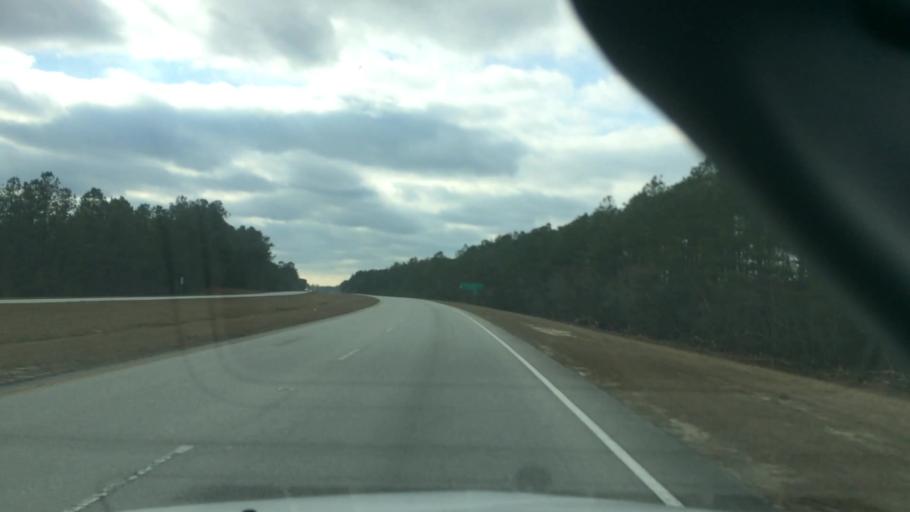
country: US
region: North Carolina
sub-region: Brunswick County
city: Bolivia
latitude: 34.0622
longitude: -78.2013
